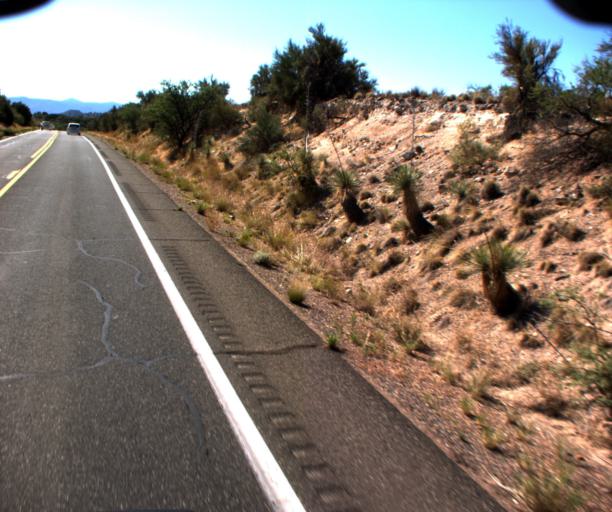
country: US
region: Arizona
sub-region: Yavapai County
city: Lake Montezuma
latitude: 34.7029
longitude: -111.7686
